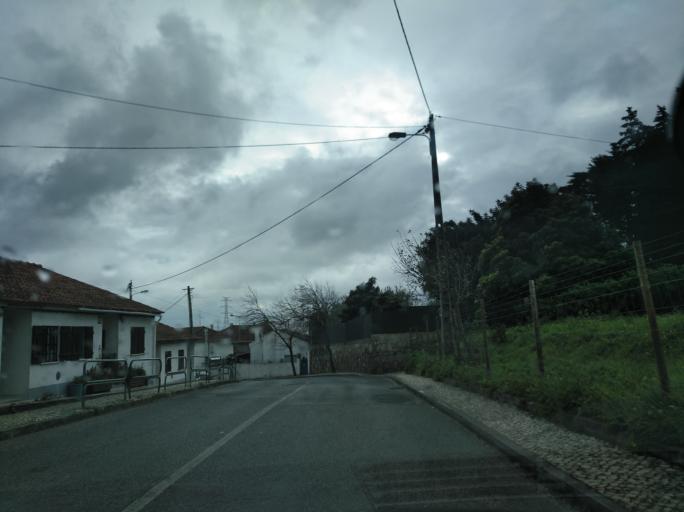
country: PT
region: Lisbon
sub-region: Odivelas
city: Famoes
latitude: 38.7890
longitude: -9.2092
